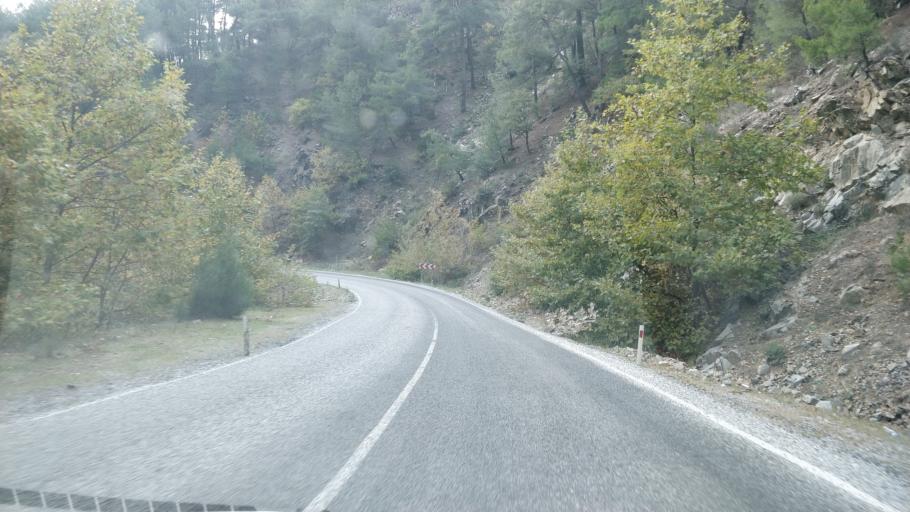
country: TR
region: Izmir
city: Kozak
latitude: 39.2191
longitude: 27.1405
